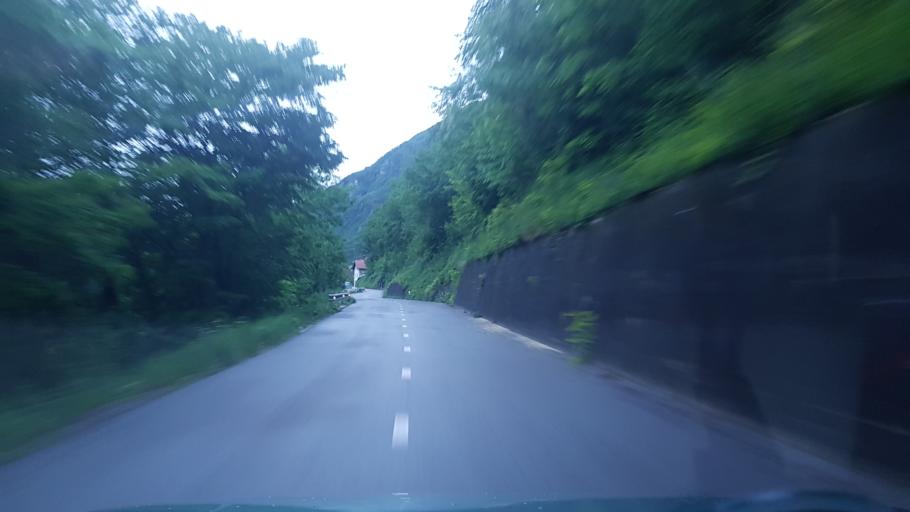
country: SI
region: Cerkno
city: Cerkno
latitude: 46.1634
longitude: 13.8891
